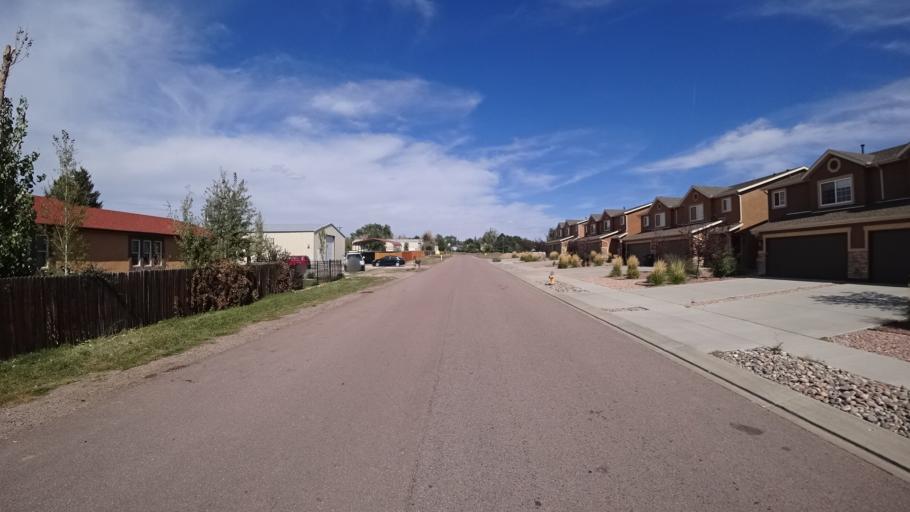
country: US
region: Colorado
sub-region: El Paso County
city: Cimarron Hills
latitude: 38.8929
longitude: -104.7497
